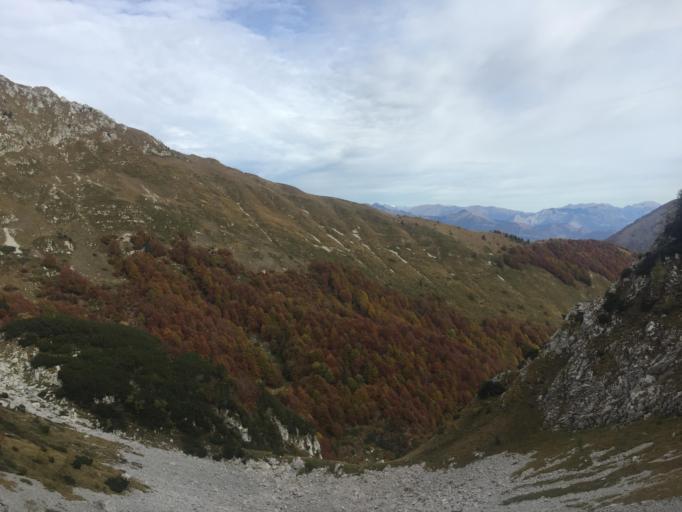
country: IT
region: Friuli Venezia Giulia
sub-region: Provincia di Udine
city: Preone
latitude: 46.3434
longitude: 12.8453
